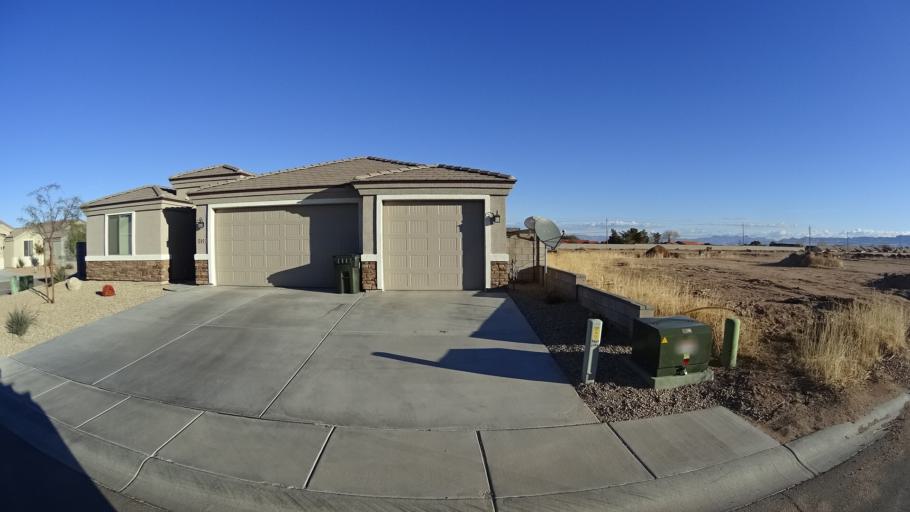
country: US
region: Arizona
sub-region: Mohave County
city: New Kingman-Butler
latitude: 35.2238
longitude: -113.9908
